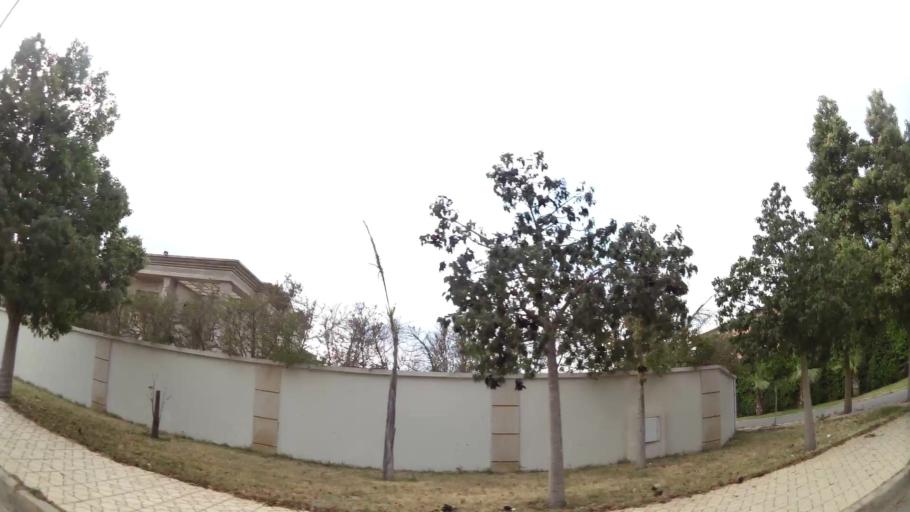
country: MA
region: Rabat-Sale-Zemmour-Zaer
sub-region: Rabat
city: Rabat
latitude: 33.9500
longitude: -6.8440
